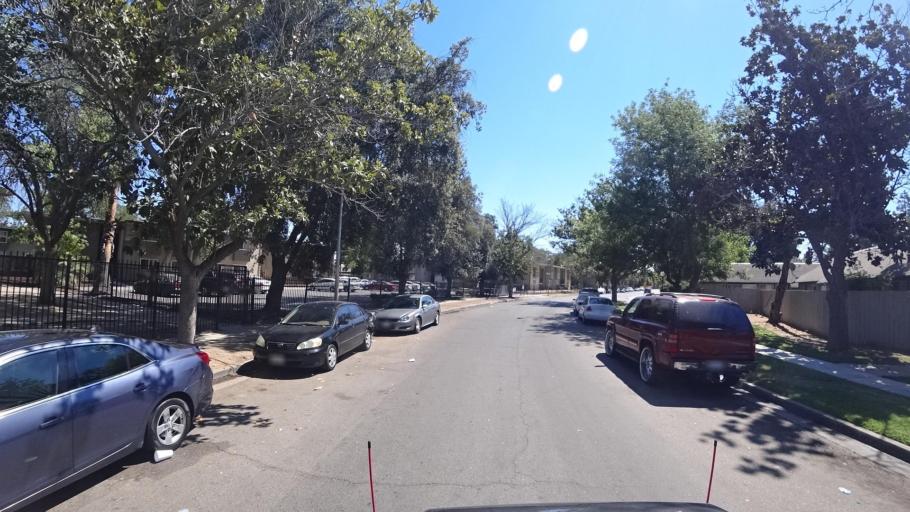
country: US
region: California
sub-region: Fresno County
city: Fresno
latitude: 36.7417
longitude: -119.7751
